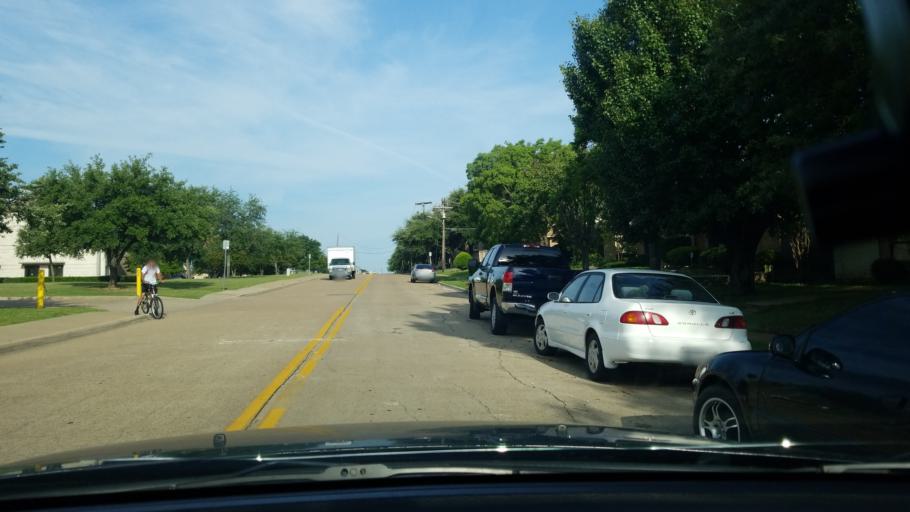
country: US
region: Texas
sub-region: Dallas County
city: Mesquite
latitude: 32.8083
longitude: -96.6078
